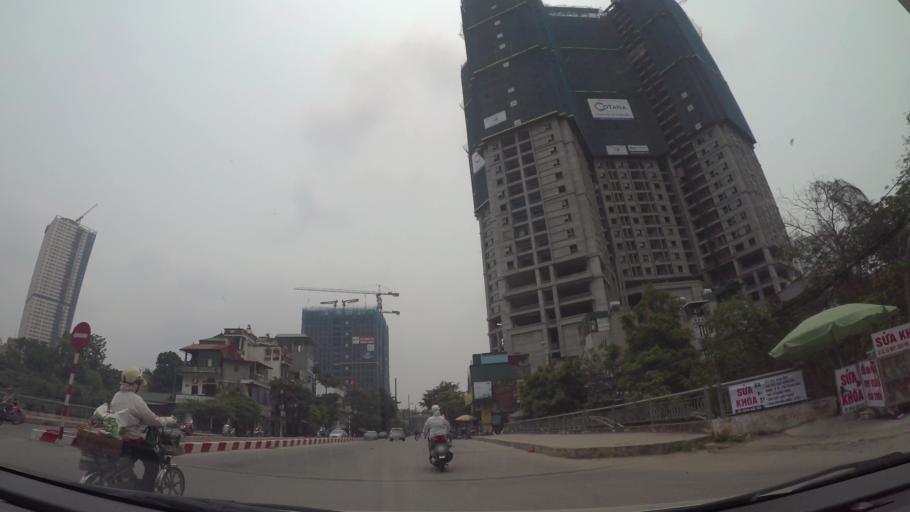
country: VN
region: Ha Noi
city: Ha Dong
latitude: 20.9759
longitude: 105.7766
